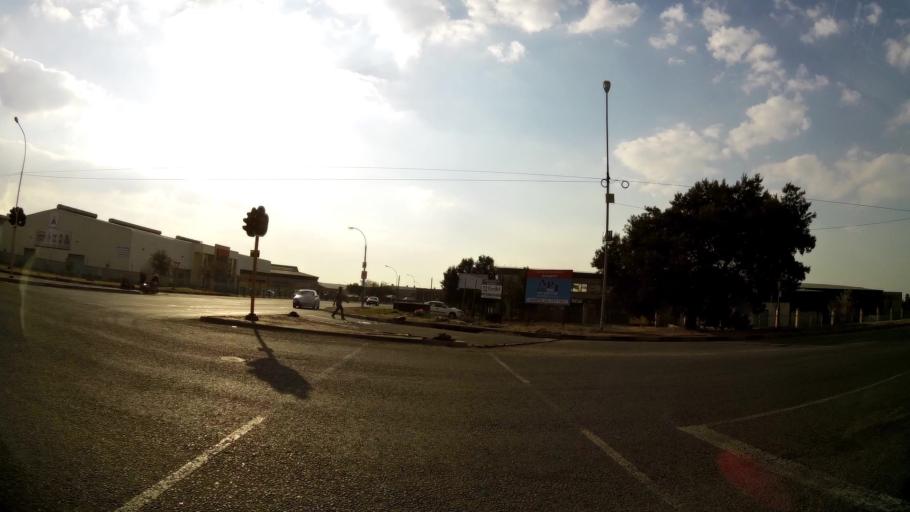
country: ZA
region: Gauteng
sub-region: City of Johannesburg Metropolitan Municipality
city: Modderfontein
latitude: -26.1195
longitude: 28.2053
